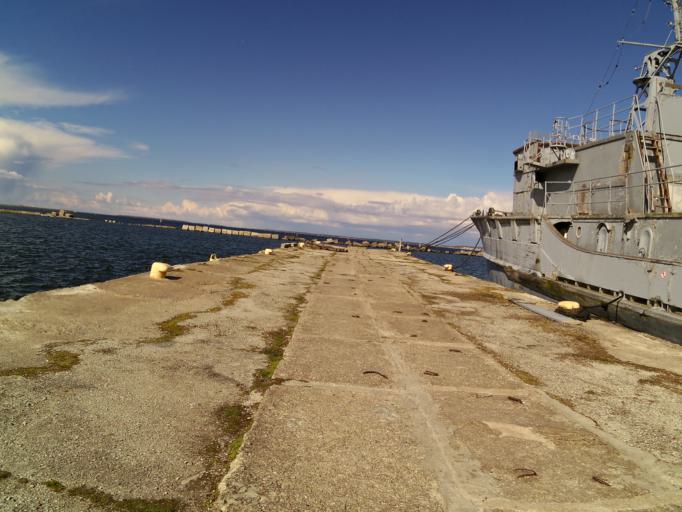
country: EE
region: Harju
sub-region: Tallinna linn
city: Tallinn
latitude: 59.4542
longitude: 24.7297
